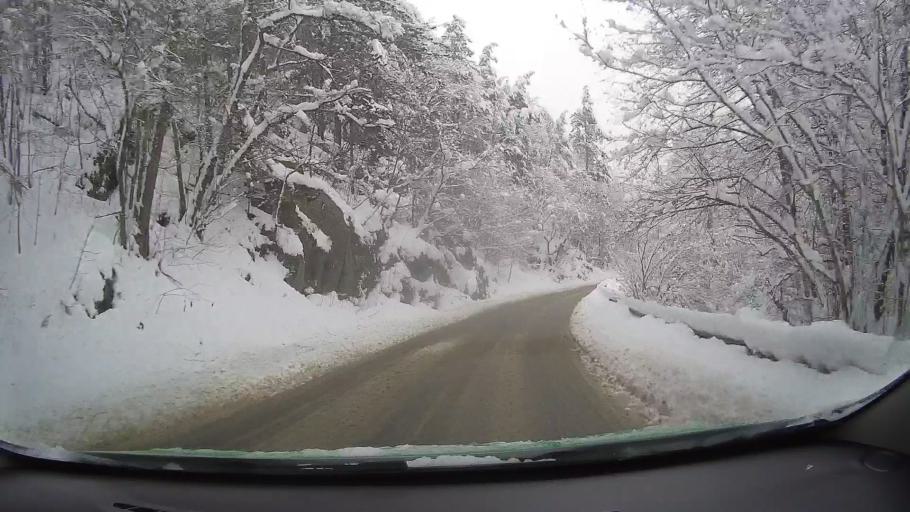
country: RO
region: Sibiu
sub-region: Comuna Tilisca
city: Tilisca
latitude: 45.8029
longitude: 23.8191
